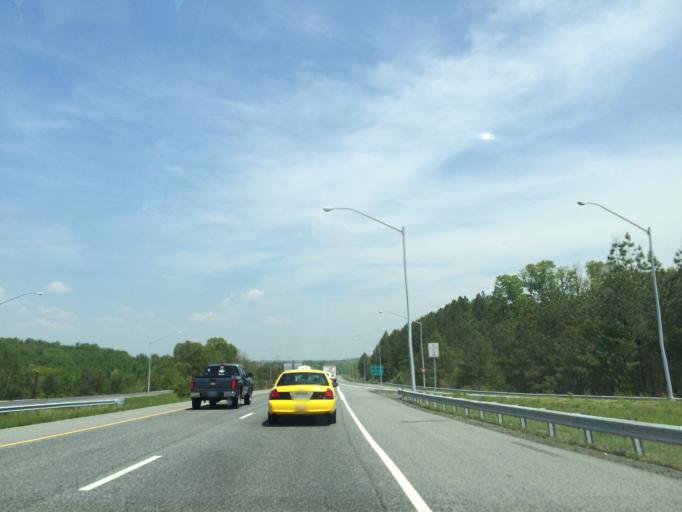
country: US
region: Maryland
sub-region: Howard County
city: Elkridge
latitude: 39.2051
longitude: -76.6957
